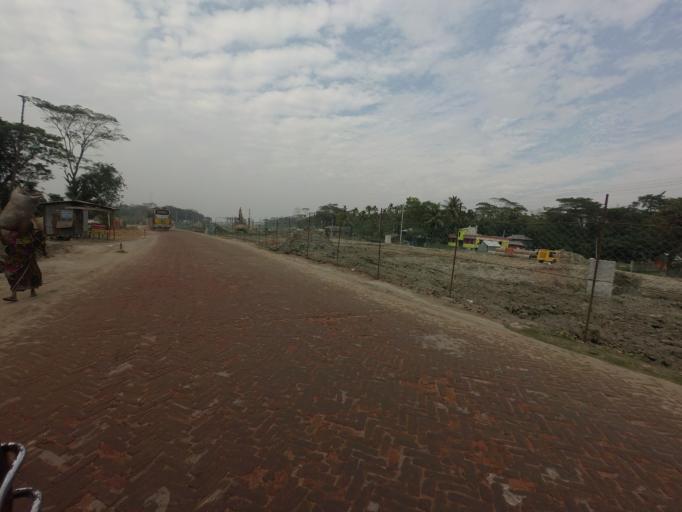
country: BD
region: Barisal
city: Nalchiti
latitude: 22.4581
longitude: 90.3407
